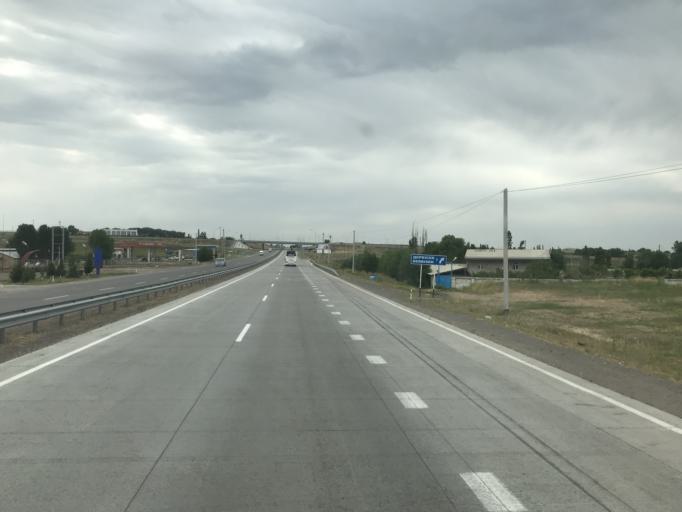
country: UZ
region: Toshkent
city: Salor
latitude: 41.5021
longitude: 69.3620
